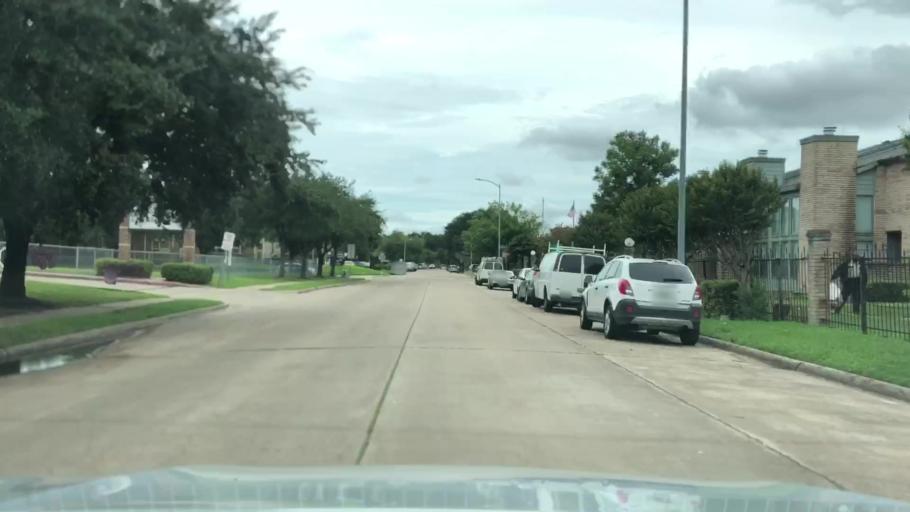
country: US
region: Texas
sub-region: Fort Bend County
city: Meadows Place
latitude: 29.7006
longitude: -95.5534
